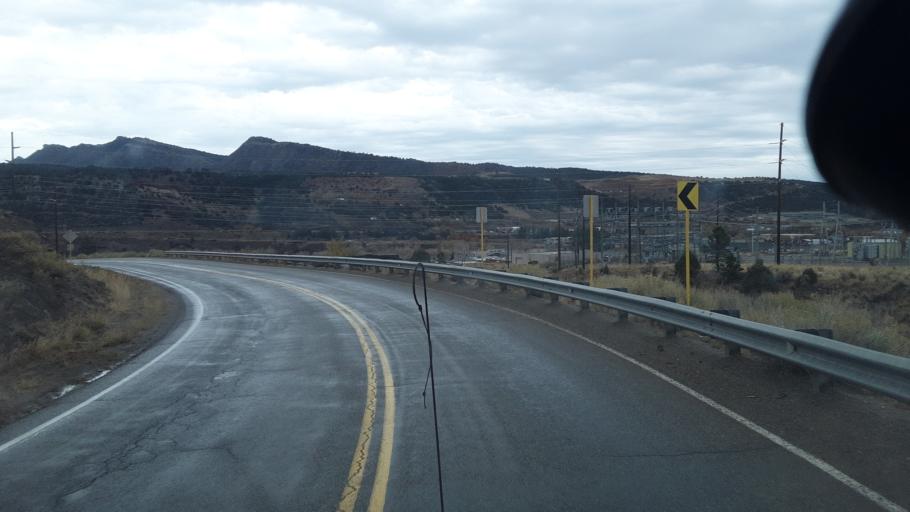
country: US
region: Colorado
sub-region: La Plata County
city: Durango
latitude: 37.2506
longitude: -107.8812
